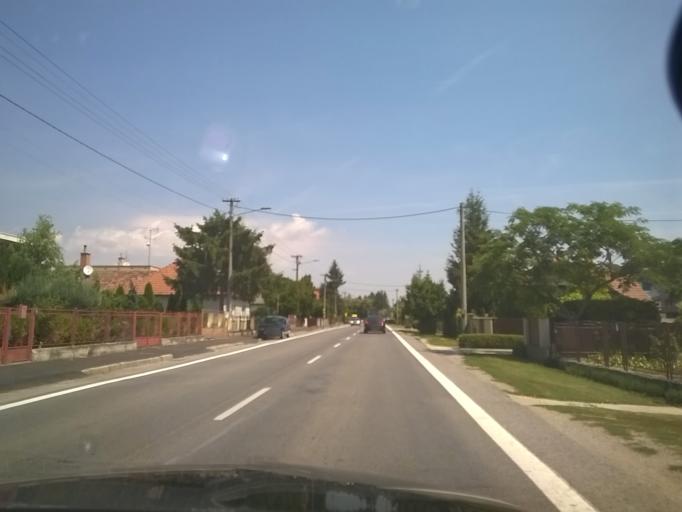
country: SK
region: Nitriansky
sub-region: Okres Nitra
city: Nitra
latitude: 48.4933
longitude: 18.1140
